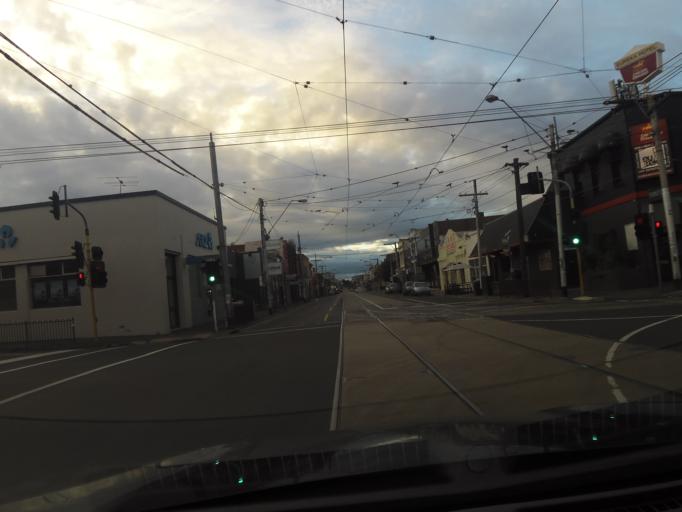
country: AU
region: Victoria
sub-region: Yarra
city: Richmond
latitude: -37.8106
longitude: 145.0004
